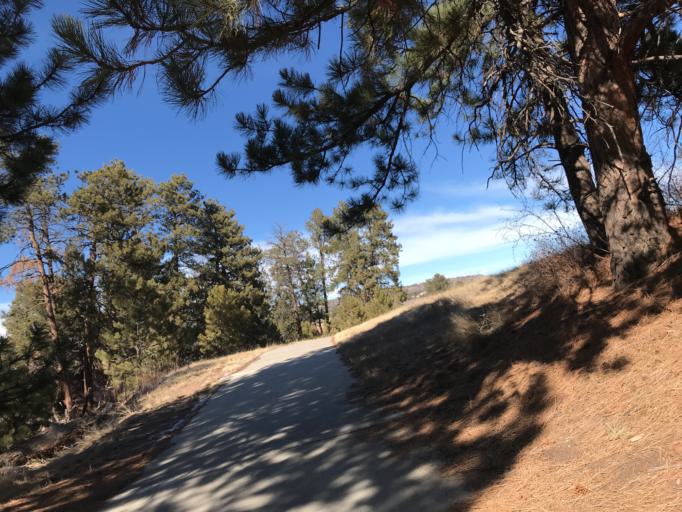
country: US
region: Colorado
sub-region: Douglas County
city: Castle Pines
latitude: 39.4108
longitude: -104.8901
